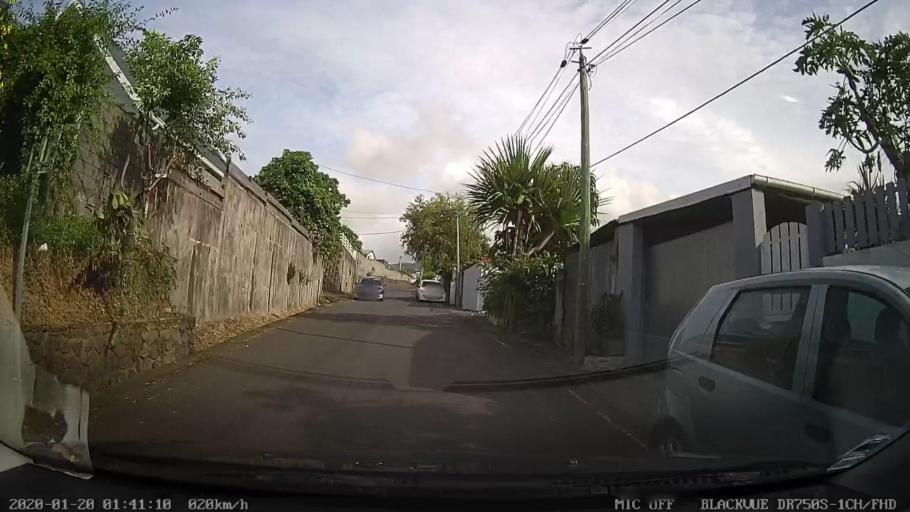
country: RE
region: Reunion
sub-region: Reunion
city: Sainte-Marie
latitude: -20.9242
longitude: 55.5169
